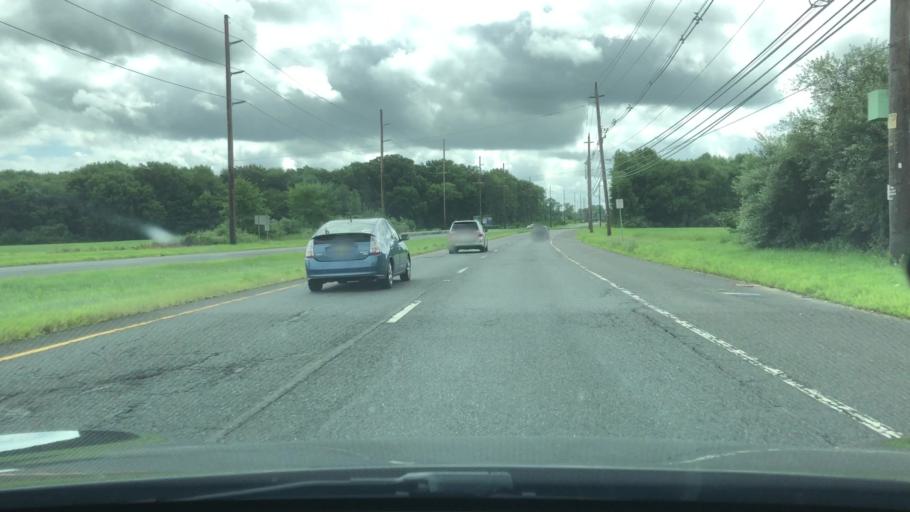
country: US
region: New Jersey
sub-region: Mercer County
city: Twin Rivers
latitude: 40.2660
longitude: -74.4582
